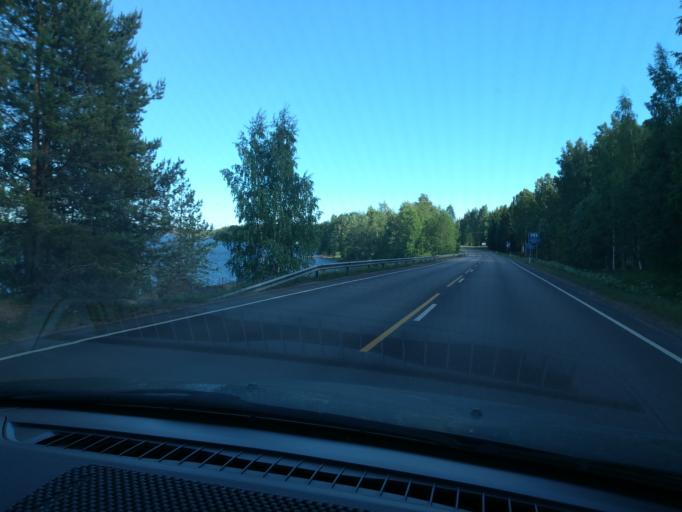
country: FI
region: Southern Savonia
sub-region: Mikkeli
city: Puumala
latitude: 61.5132
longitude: 28.1770
